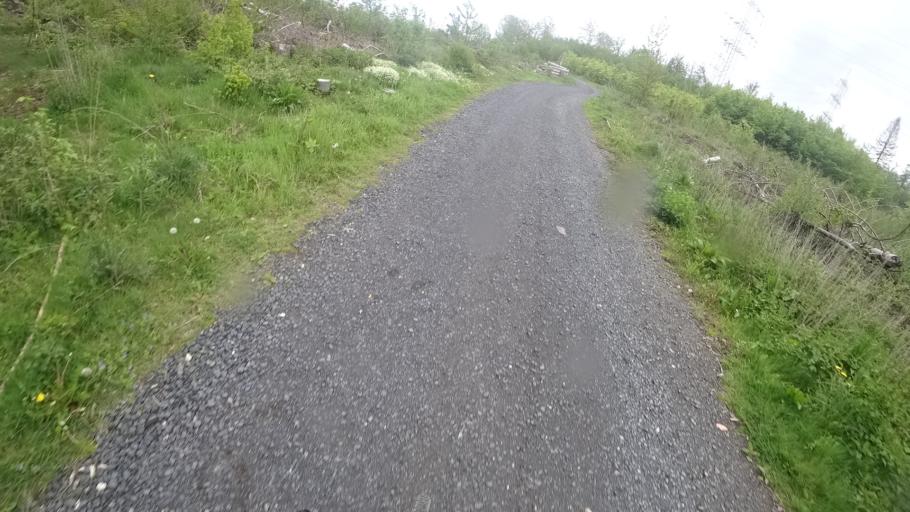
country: DE
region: Rheinland-Pfalz
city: Scheuerfeld
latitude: 50.7762
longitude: 7.8431
